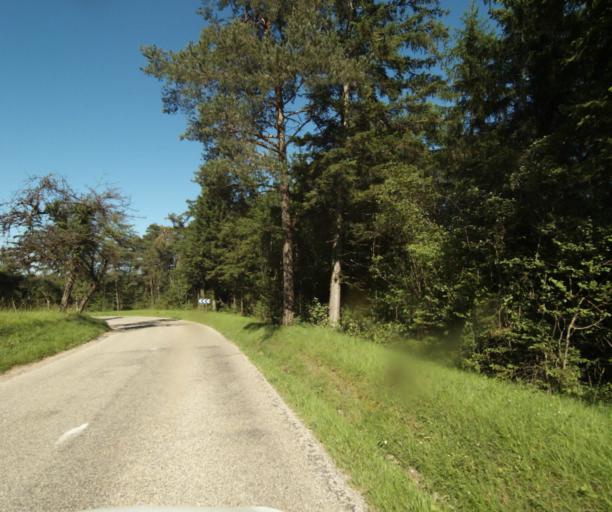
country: FR
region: Rhone-Alpes
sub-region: Departement de la Haute-Savoie
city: Sciez
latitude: 46.3169
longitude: 6.3853
